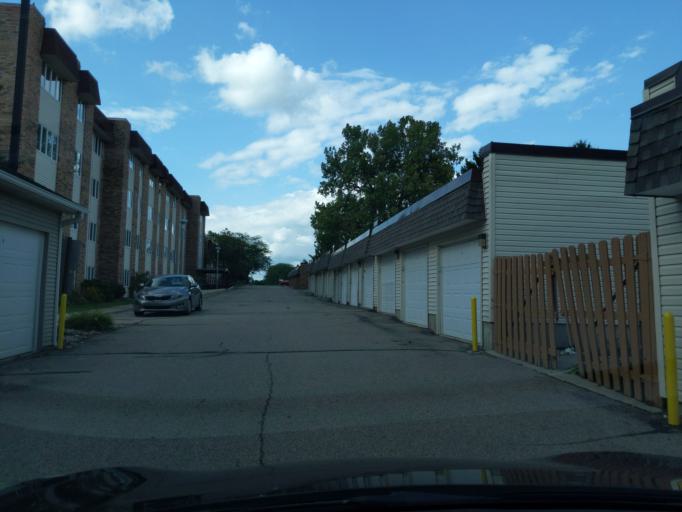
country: US
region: Michigan
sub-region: Jackson County
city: Jackson
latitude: 42.2749
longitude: -84.4406
